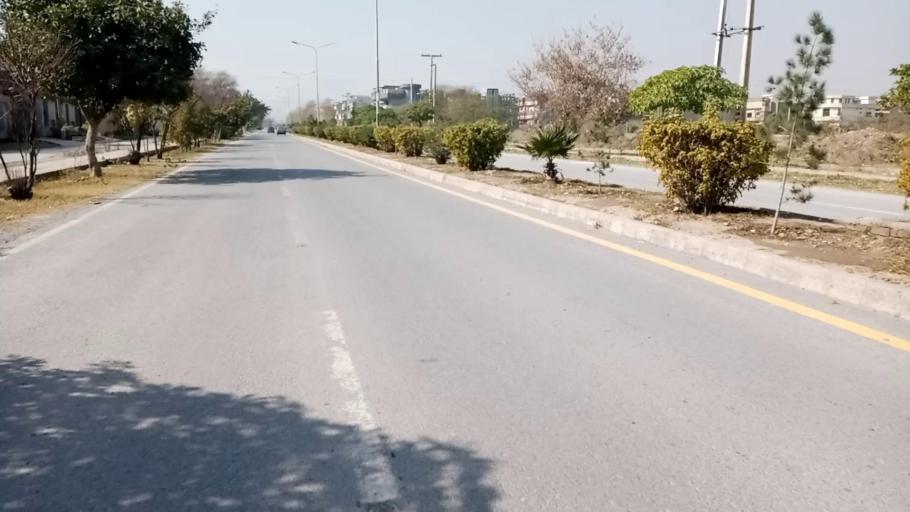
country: PK
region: Khyber Pakhtunkhwa
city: Peshawar
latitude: 33.9629
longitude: 71.4185
